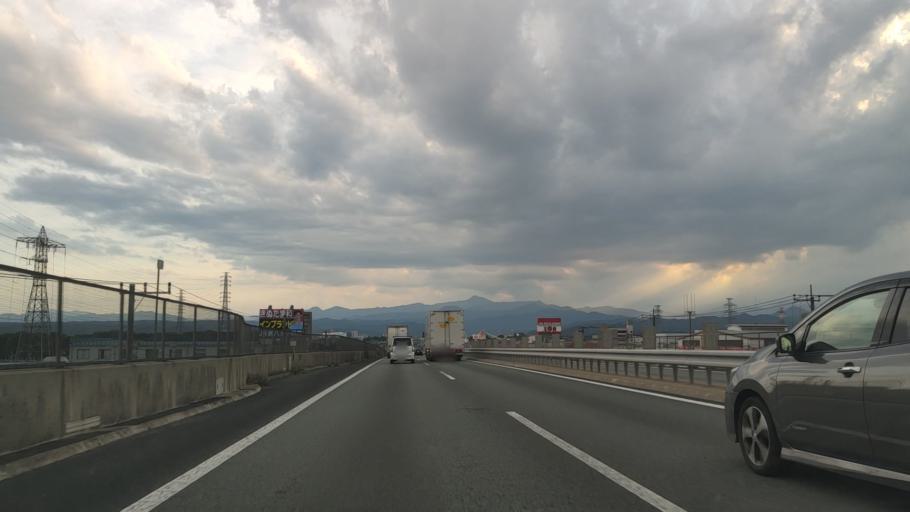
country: JP
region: Saitama
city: Hanno
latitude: 35.7953
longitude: 139.3171
